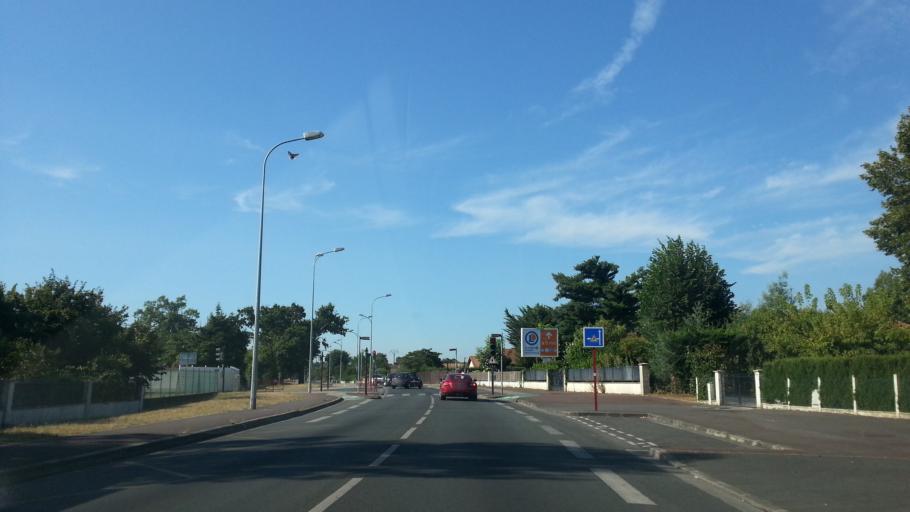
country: FR
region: Aquitaine
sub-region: Departement de la Gironde
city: Leognan
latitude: 44.7624
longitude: -0.5816
